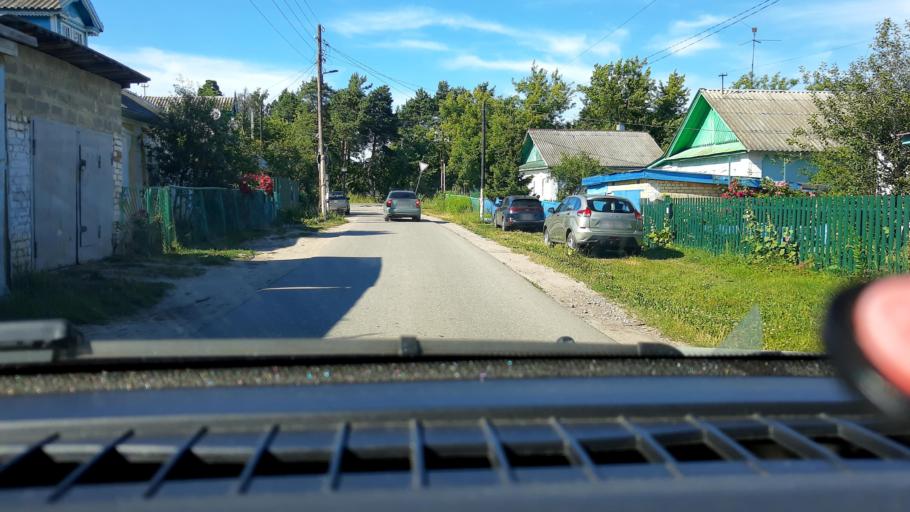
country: RU
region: Nizjnij Novgorod
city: Gorbatovka
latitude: 56.2626
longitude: 43.7463
